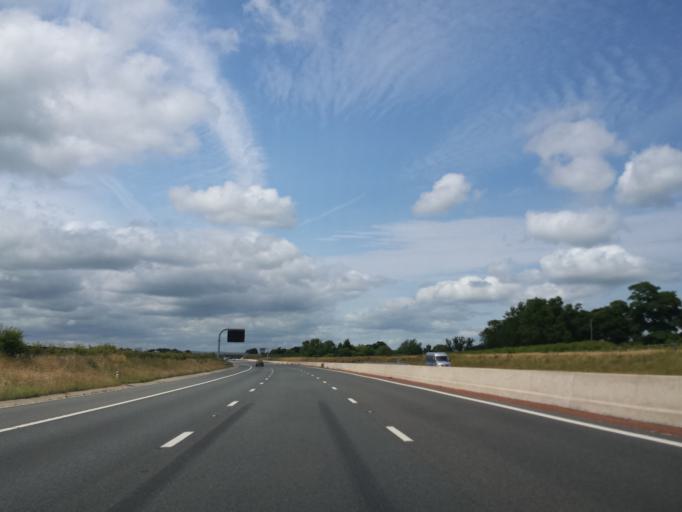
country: GB
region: England
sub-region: North Yorkshire
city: Bedale
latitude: 54.2778
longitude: -1.5319
